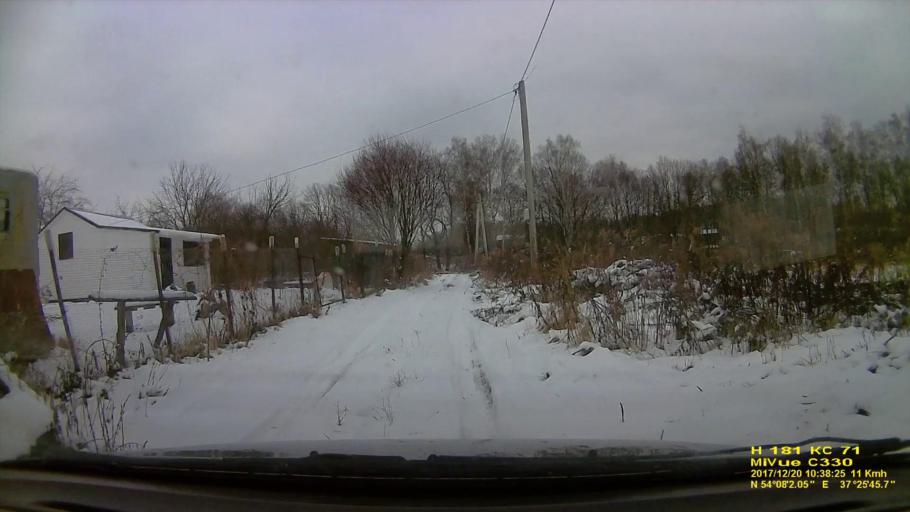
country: RU
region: Tula
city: Kosaya Gora
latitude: 54.1339
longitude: 37.4295
